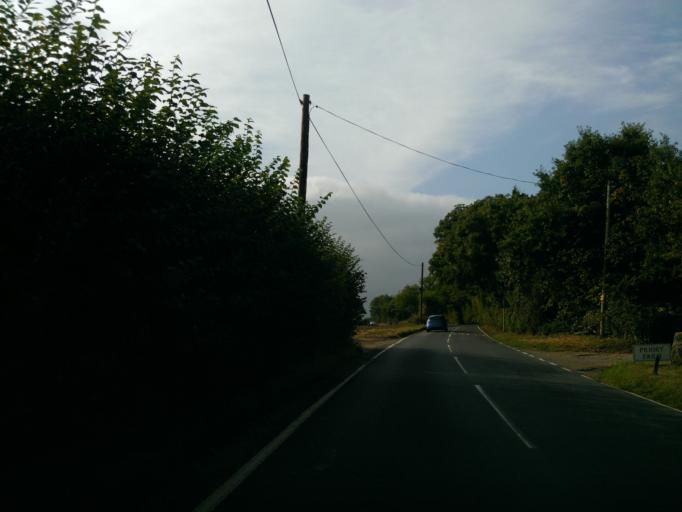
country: GB
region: England
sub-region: Essex
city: Tiptree
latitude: 51.7972
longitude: 0.7189
